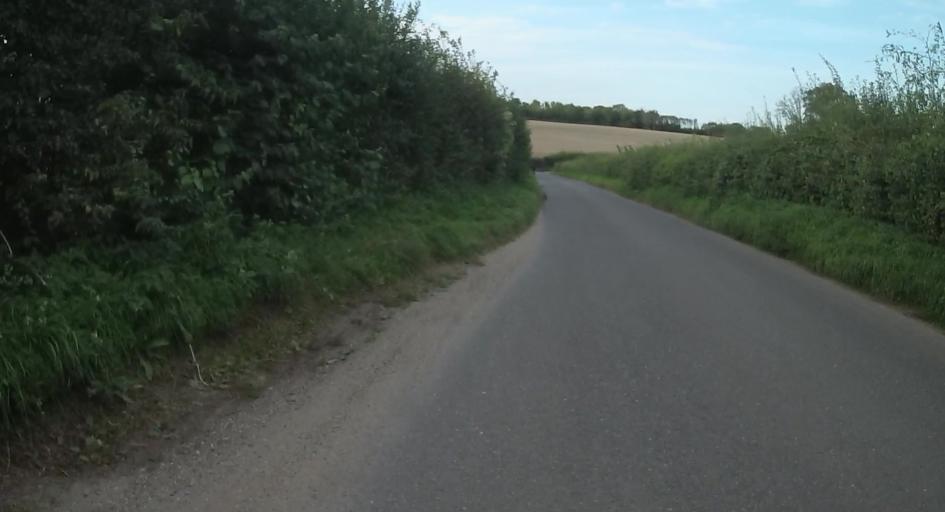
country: GB
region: England
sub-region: Hampshire
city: Kings Worthy
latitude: 51.0765
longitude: -1.1852
